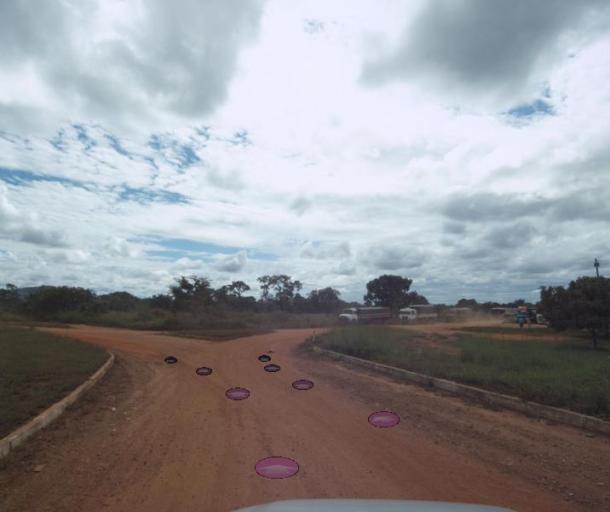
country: BR
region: Goias
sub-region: Uruacu
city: Uruacu
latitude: -14.4640
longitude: -49.1561
